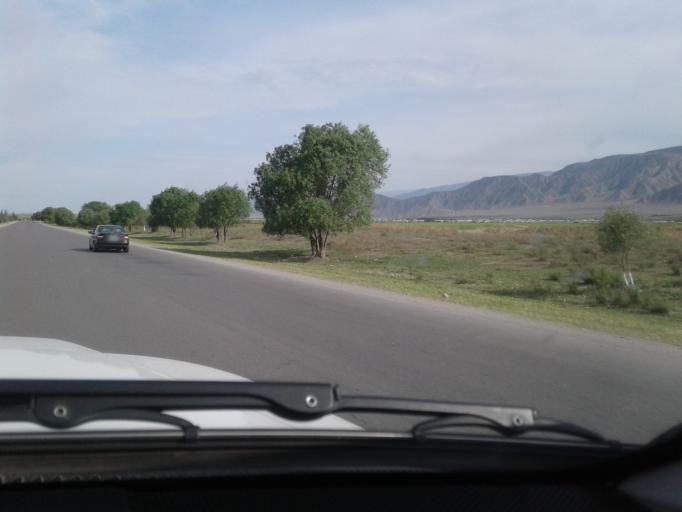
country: TM
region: Ahal
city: Arcabil
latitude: 38.1859
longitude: 57.8536
